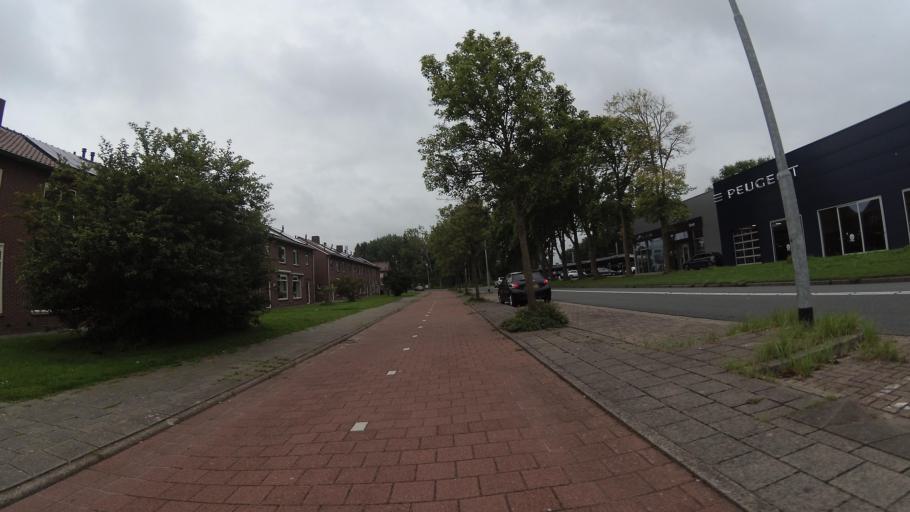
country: NL
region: North Holland
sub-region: Gemeente Den Helder
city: Den Helder
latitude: 52.9504
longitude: 4.7631
